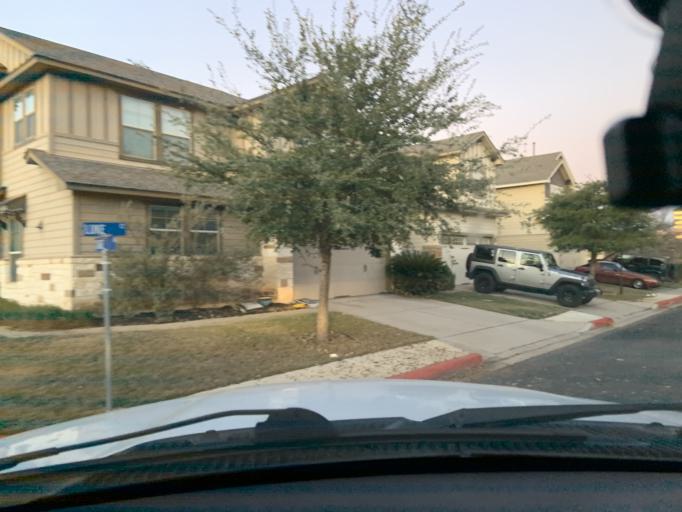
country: US
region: Texas
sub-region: Williamson County
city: Anderson Mill
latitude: 30.4626
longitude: -97.7993
